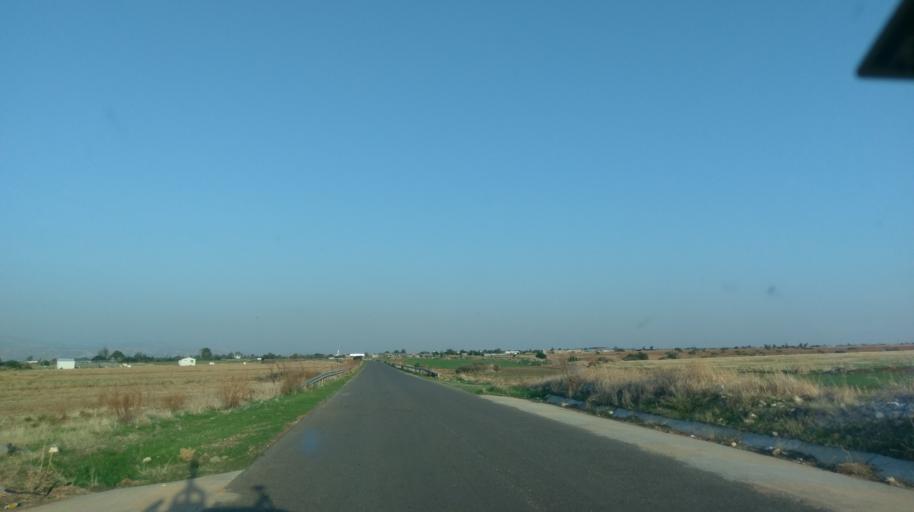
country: CY
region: Lefkosia
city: Morfou
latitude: 35.1526
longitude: 32.9880
